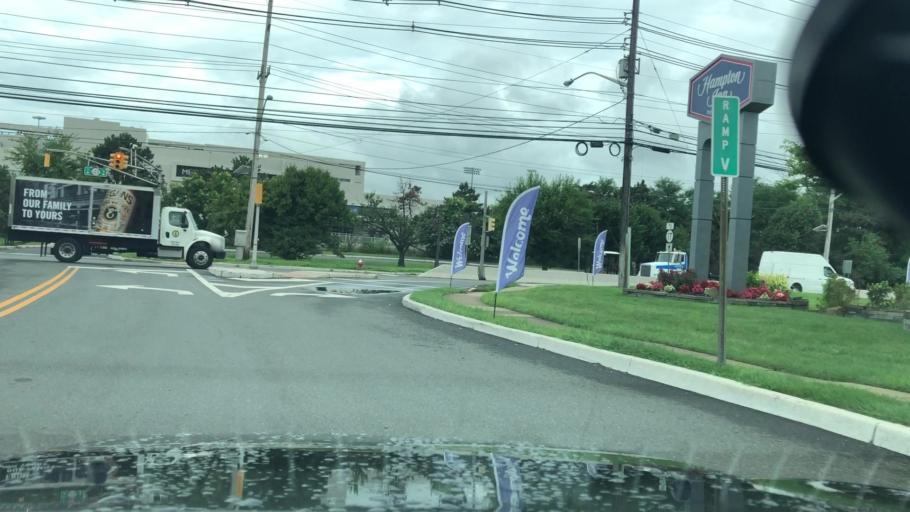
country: US
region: New Jersey
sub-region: Bergen County
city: Carlstadt
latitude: 40.8213
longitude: -74.0691
